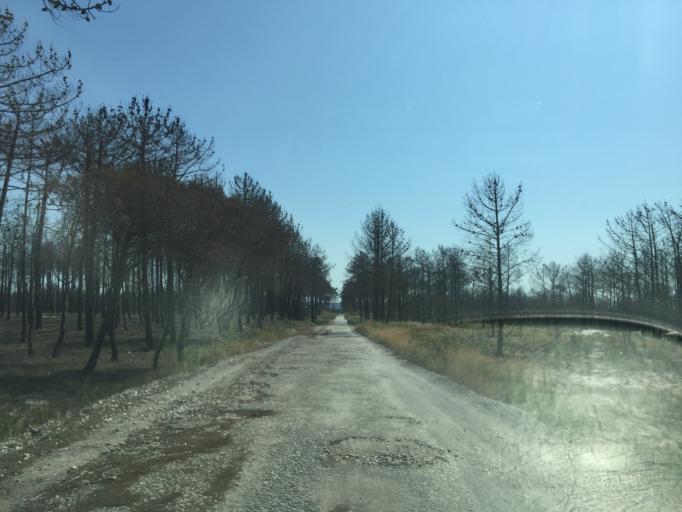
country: PT
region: Coimbra
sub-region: Figueira da Foz
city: Alhadas
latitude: 40.2671
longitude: -8.8319
